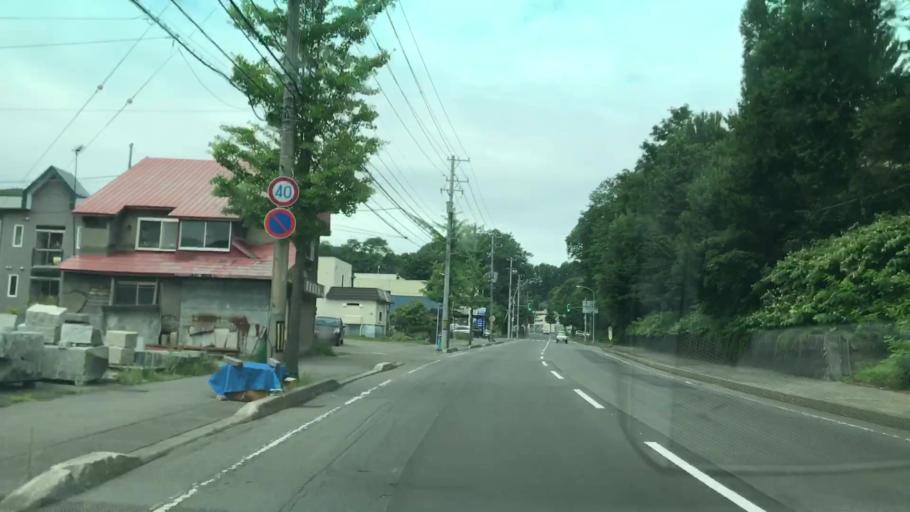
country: JP
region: Hokkaido
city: Otaru
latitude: 43.2103
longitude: 140.9688
